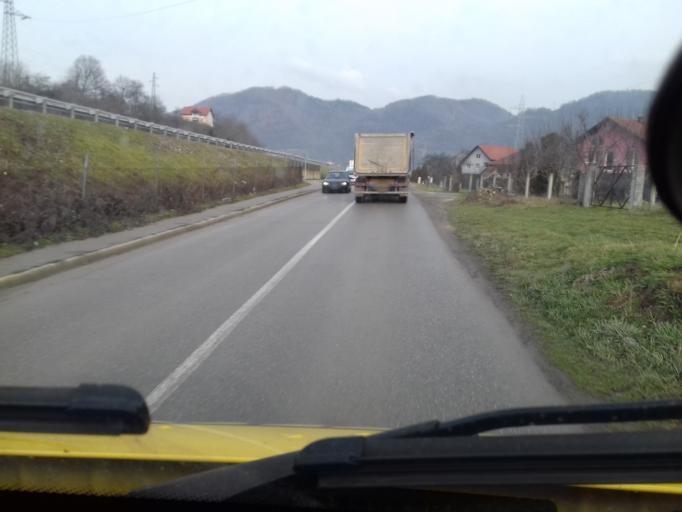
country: BA
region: Federation of Bosnia and Herzegovina
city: Dobrinje
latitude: 44.0379
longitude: 18.1221
